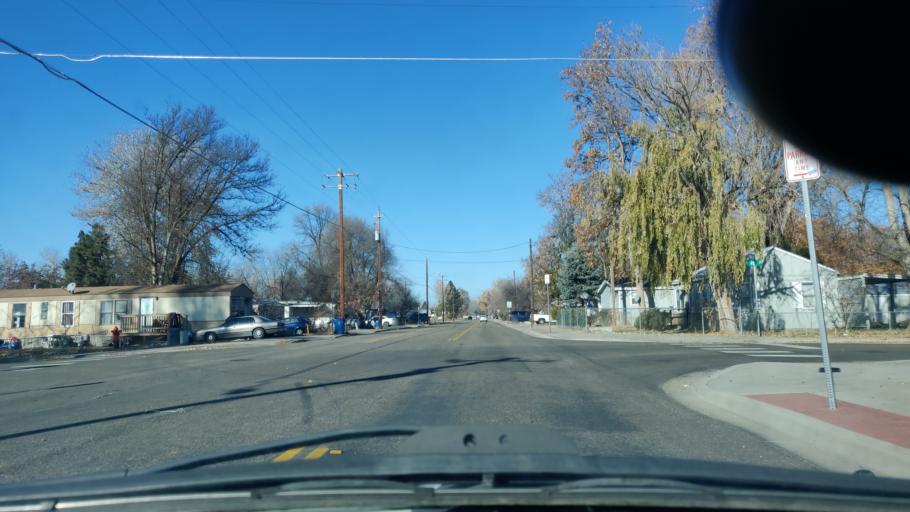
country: US
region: Idaho
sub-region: Ada County
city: Garden City
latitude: 43.6418
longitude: -116.2574
